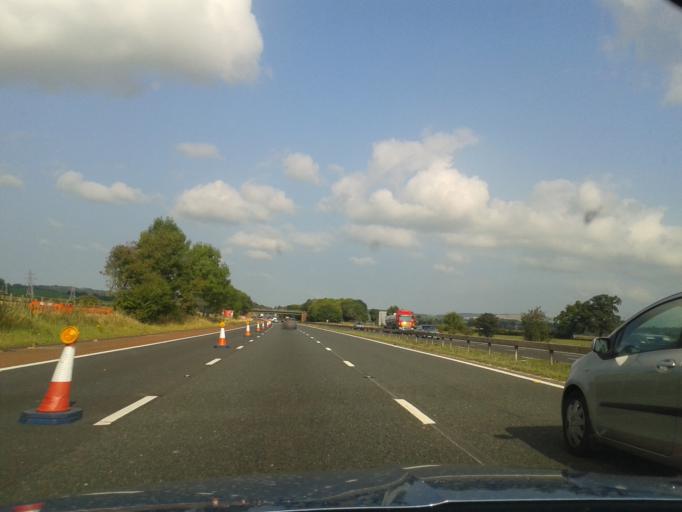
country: GB
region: England
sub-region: Cumbria
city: Penrith
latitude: 54.7108
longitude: -2.7944
